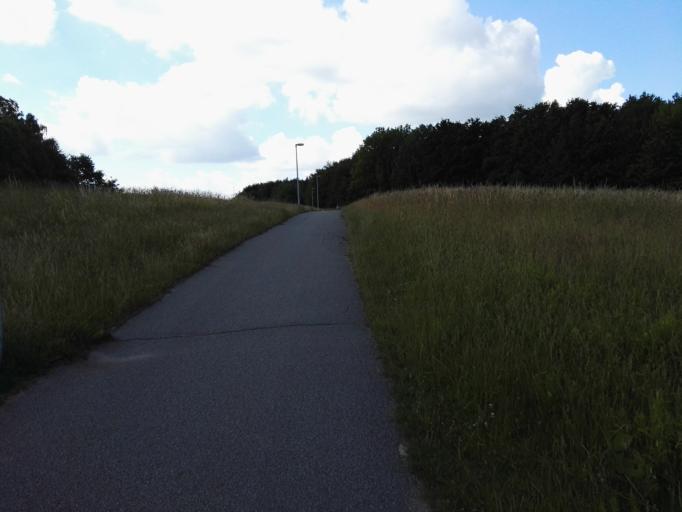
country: DK
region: Capital Region
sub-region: Ballerup Kommune
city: Ballerup
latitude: 55.7385
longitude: 12.3962
